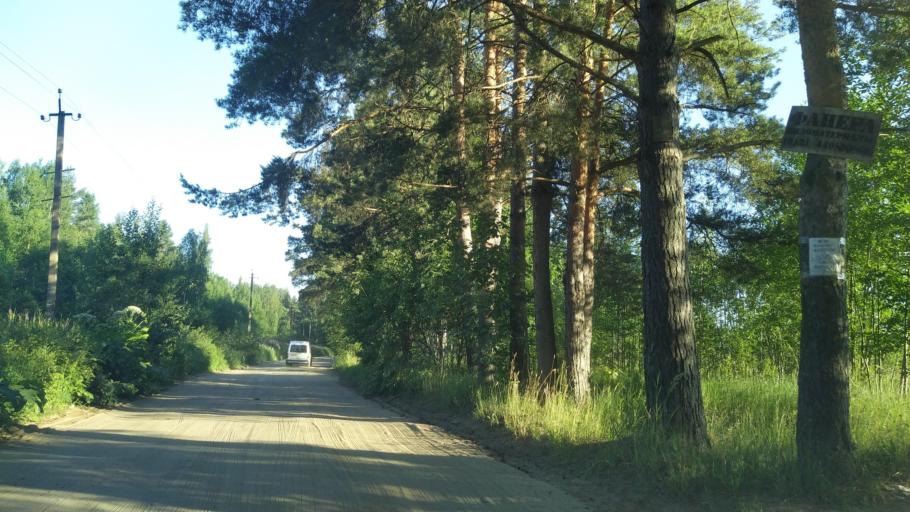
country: RU
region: Leningrad
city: Koltushi
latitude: 59.9100
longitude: 30.7362
